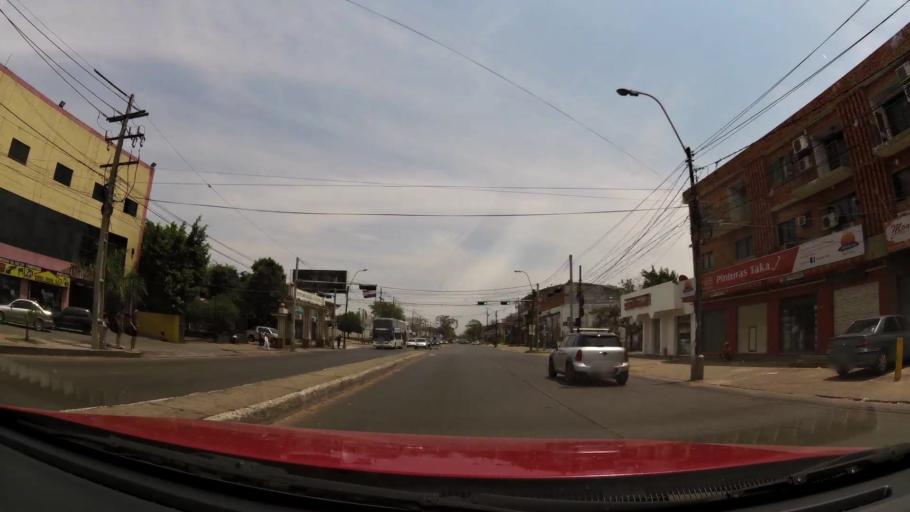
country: PY
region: Central
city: Lambare
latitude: -25.3148
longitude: -57.5787
